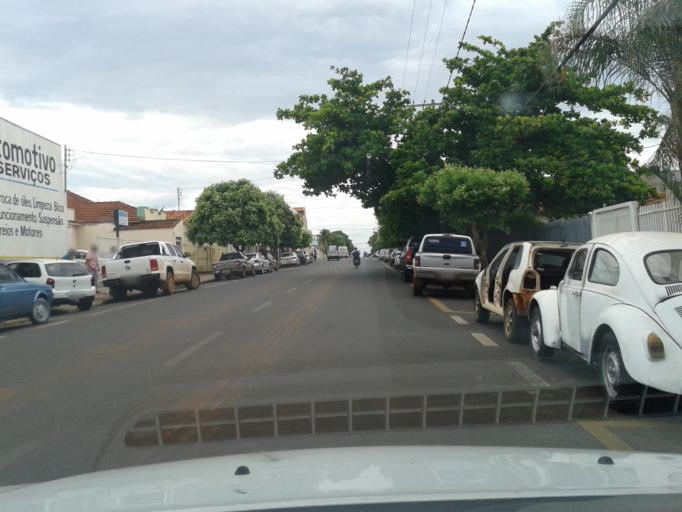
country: BR
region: Minas Gerais
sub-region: Iturama
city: Iturama
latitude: -19.7319
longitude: -50.1965
